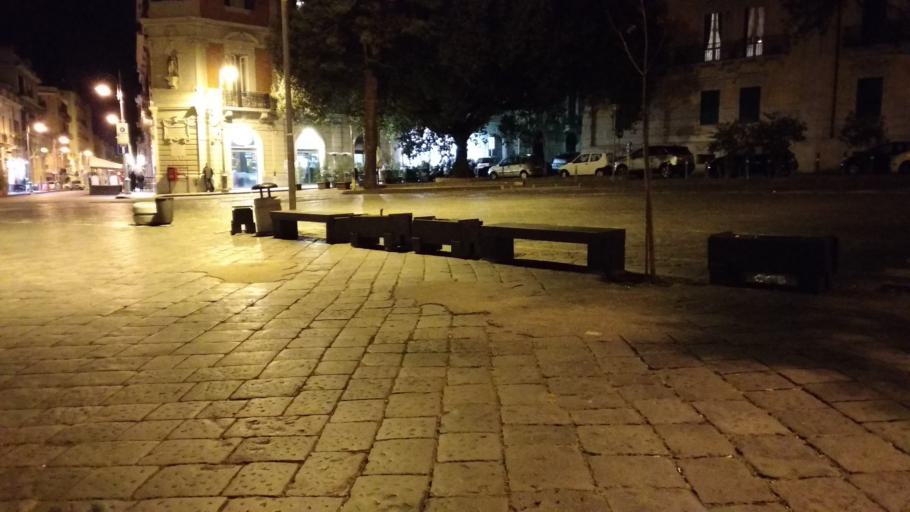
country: IT
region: Sicily
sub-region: Messina
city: Messina
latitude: 38.1919
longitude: 15.5547
